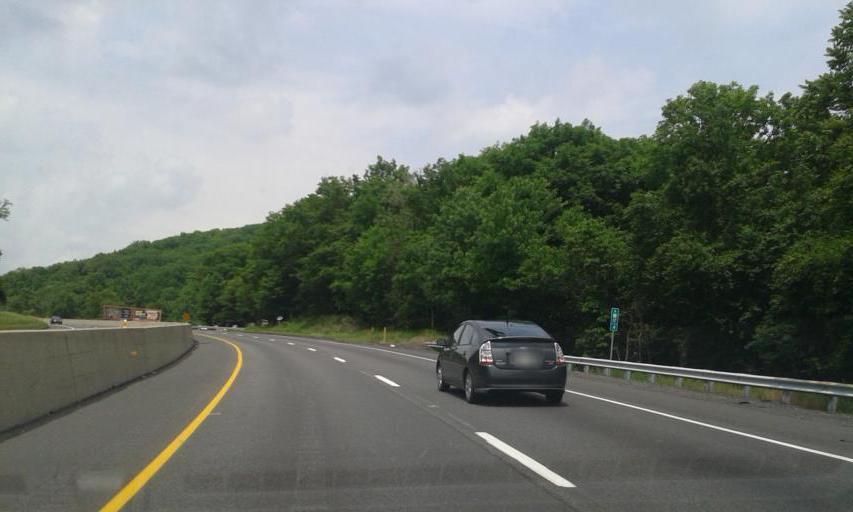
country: US
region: Pennsylvania
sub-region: Northampton County
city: Wind Gap
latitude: 40.8583
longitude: -75.2944
